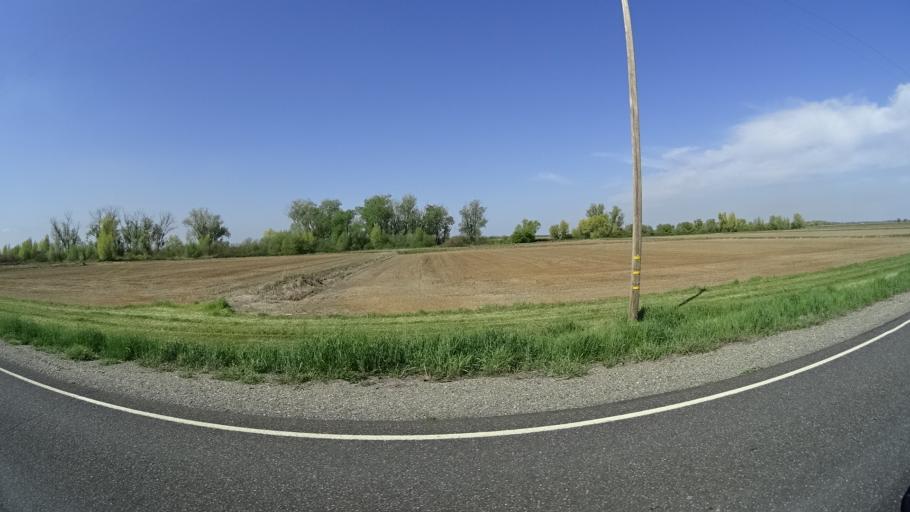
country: US
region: California
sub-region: Butte County
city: Durham
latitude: 39.4830
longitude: -121.9292
